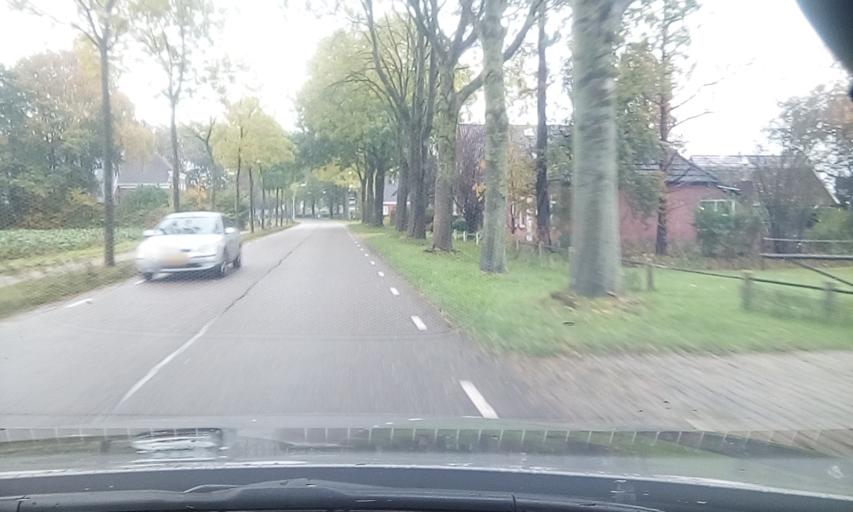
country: NL
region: Groningen
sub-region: Gemeente Haren
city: Haren
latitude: 53.2092
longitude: 6.6773
